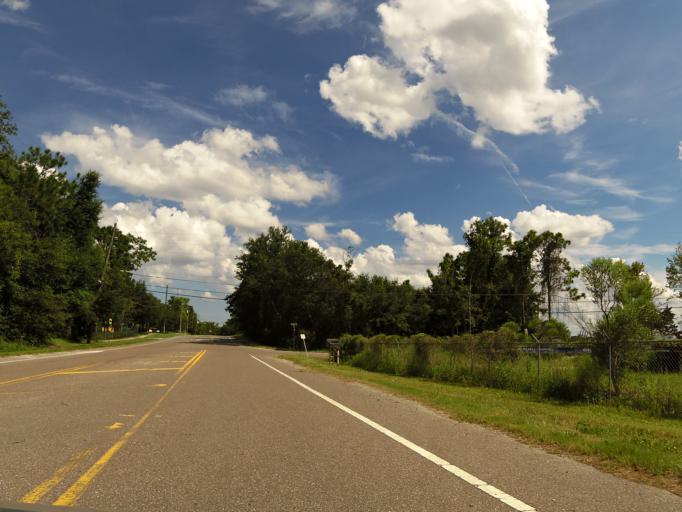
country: US
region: Florida
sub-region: Duval County
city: Jacksonville
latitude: 30.4229
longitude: -81.5732
